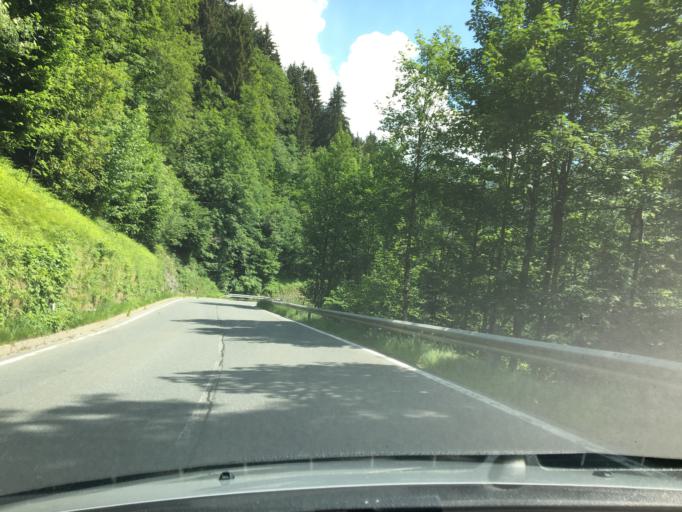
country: AT
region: Salzburg
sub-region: Politischer Bezirk Sankt Johann im Pongau
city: Sankt Johann im Pongau
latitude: 47.3420
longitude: 13.2112
